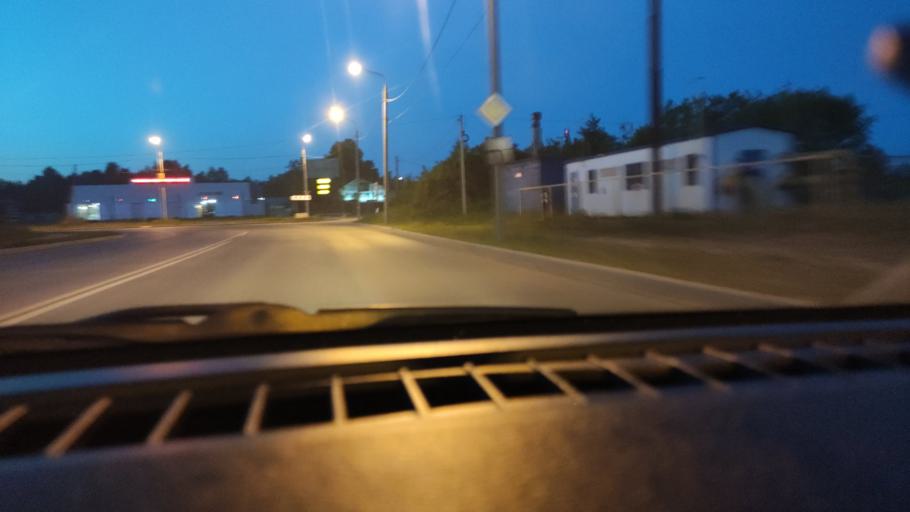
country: RU
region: Perm
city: Kondratovo
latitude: 57.9548
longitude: 56.1852
